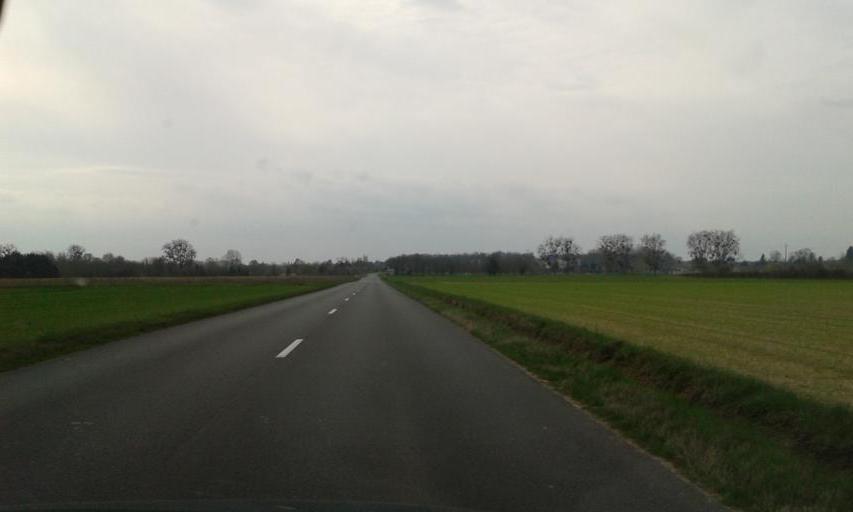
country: FR
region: Centre
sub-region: Departement du Loiret
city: Meung-sur-Loire
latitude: 47.8228
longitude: 1.7132
